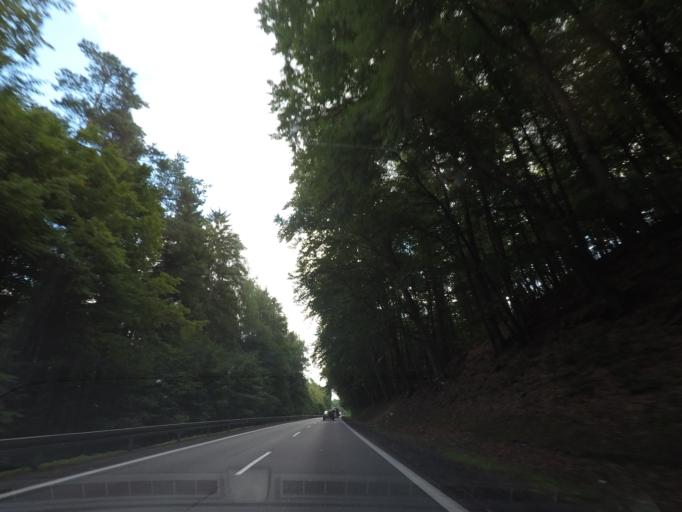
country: PL
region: Pomeranian Voivodeship
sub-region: Powiat wejherowski
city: Leczyce
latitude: 54.5734
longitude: 17.9273
